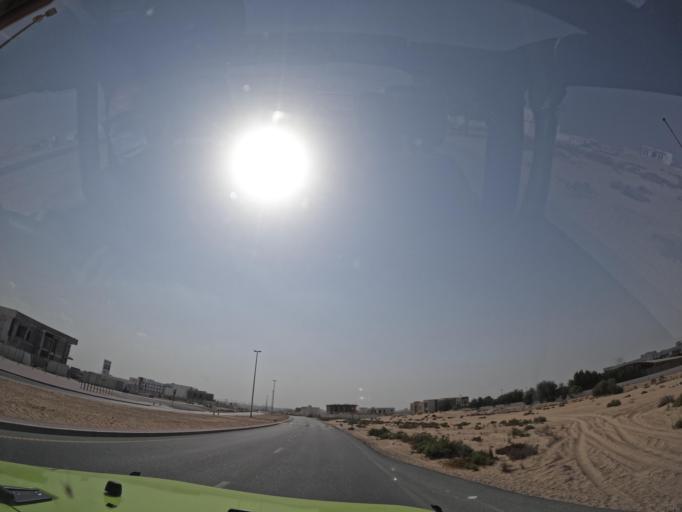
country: AE
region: Ash Shariqah
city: Sharjah
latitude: 25.1939
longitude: 55.4290
